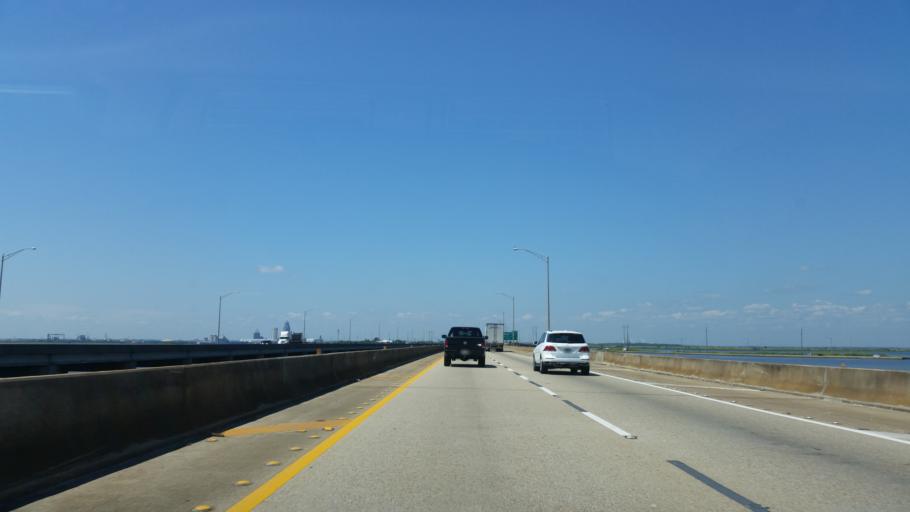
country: US
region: Alabama
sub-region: Baldwin County
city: Spanish Fort
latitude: 30.6721
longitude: -87.9781
